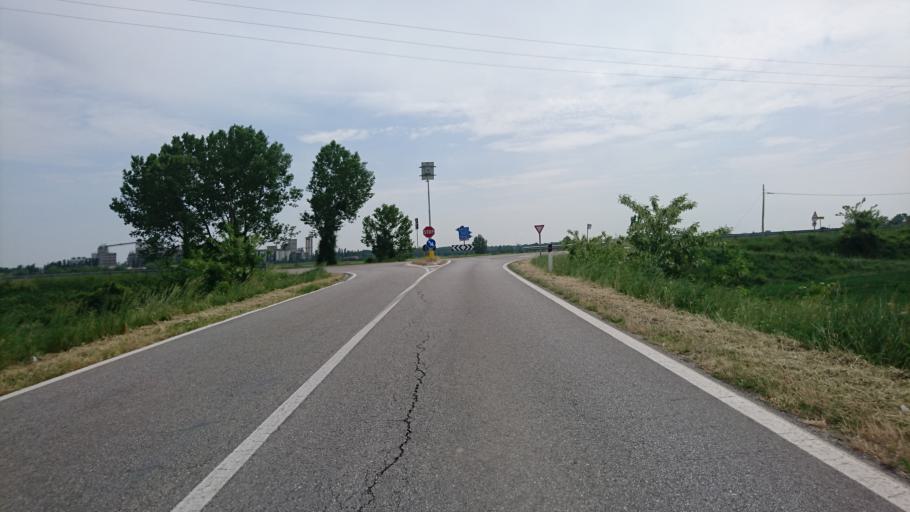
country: IT
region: Veneto
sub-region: Provincia di Padova
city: Arqua Petrarca
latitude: 45.2495
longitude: 11.7172
